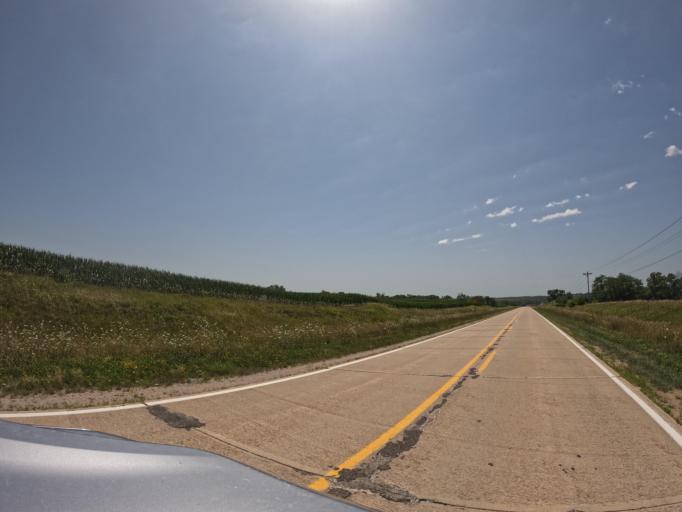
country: US
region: Iowa
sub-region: Henry County
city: Mount Pleasant
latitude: 40.9119
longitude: -91.5543
